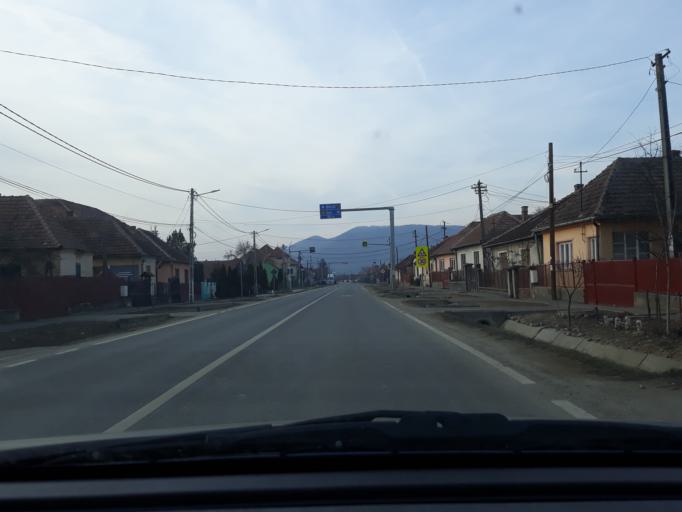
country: RO
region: Salaj
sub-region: Comuna Periceiu
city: Periceiu
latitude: 47.2256
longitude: 22.8629
